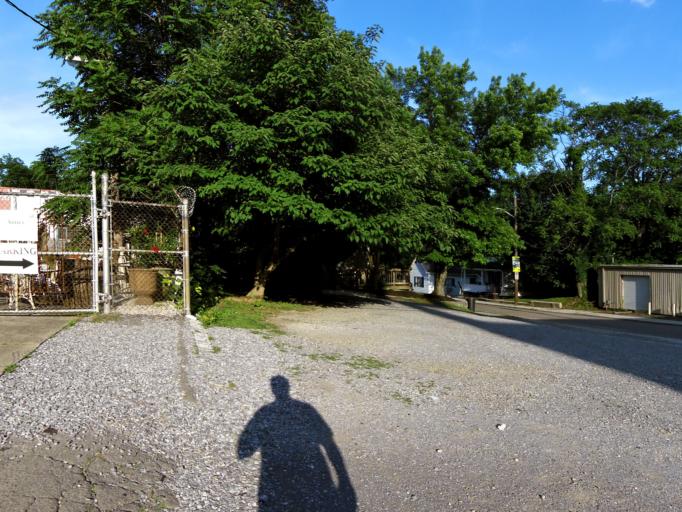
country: US
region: Tennessee
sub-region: Knox County
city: Knoxville
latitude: 35.9788
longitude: -83.9235
